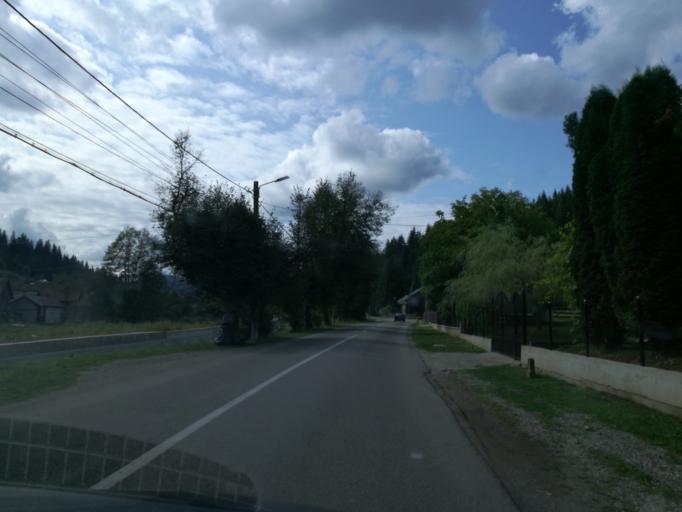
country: RO
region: Suceava
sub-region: Oras Gura Humorului
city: Gura Humorului
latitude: 47.5316
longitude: 25.8643
